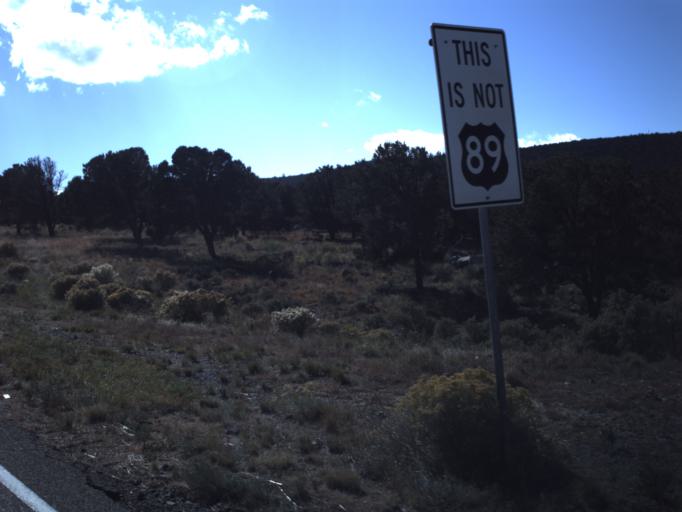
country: US
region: Utah
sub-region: Garfield County
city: Panguitch
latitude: 37.8016
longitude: -112.4357
